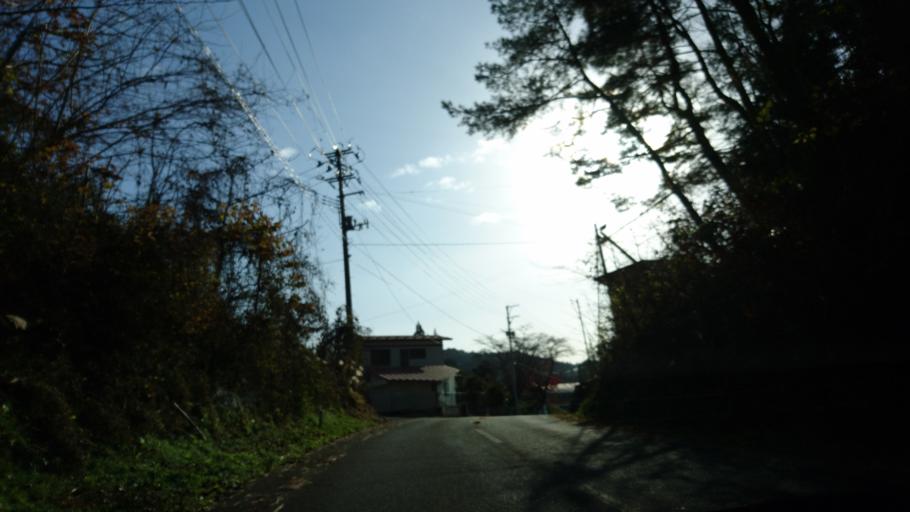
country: JP
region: Iwate
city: Ichinoseki
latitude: 38.8615
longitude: 141.3411
